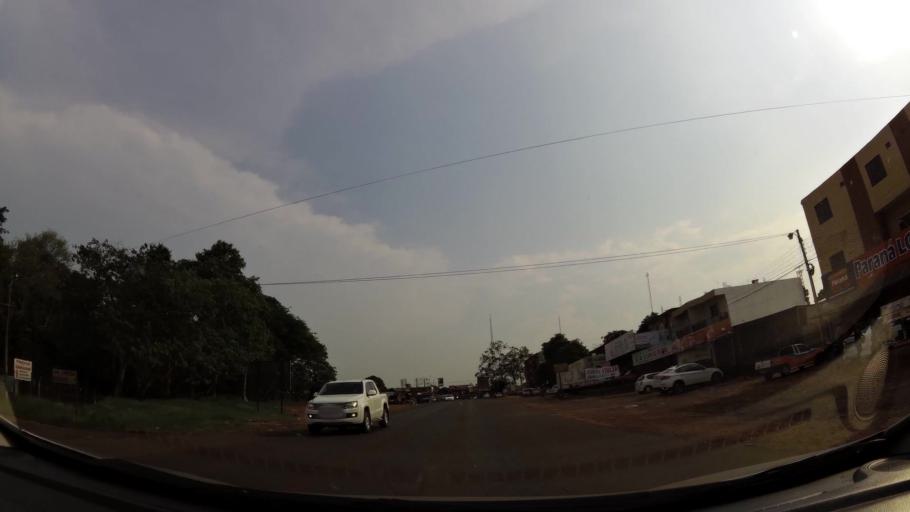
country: PY
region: Alto Parana
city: Ciudad del Este
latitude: -25.4968
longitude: -54.6628
